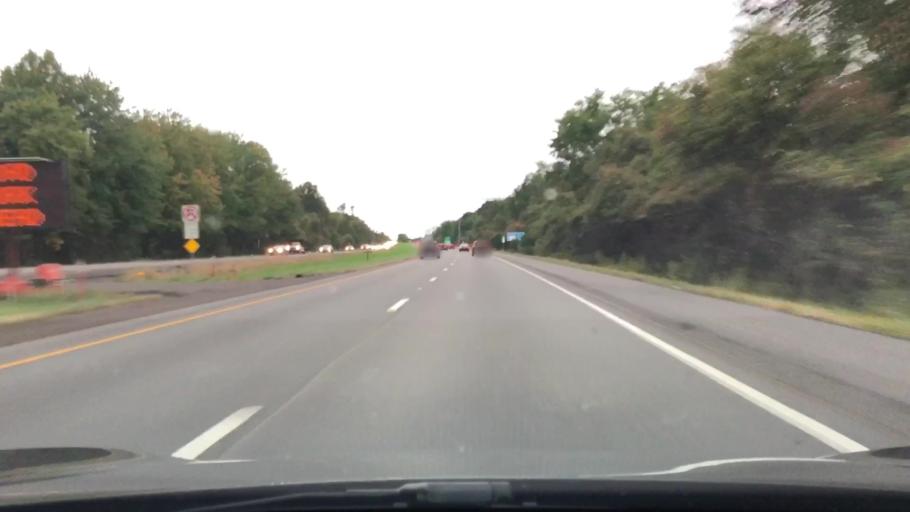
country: US
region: Pennsylvania
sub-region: Bucks County
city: Woodside
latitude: 40.2111
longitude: -74.8760
